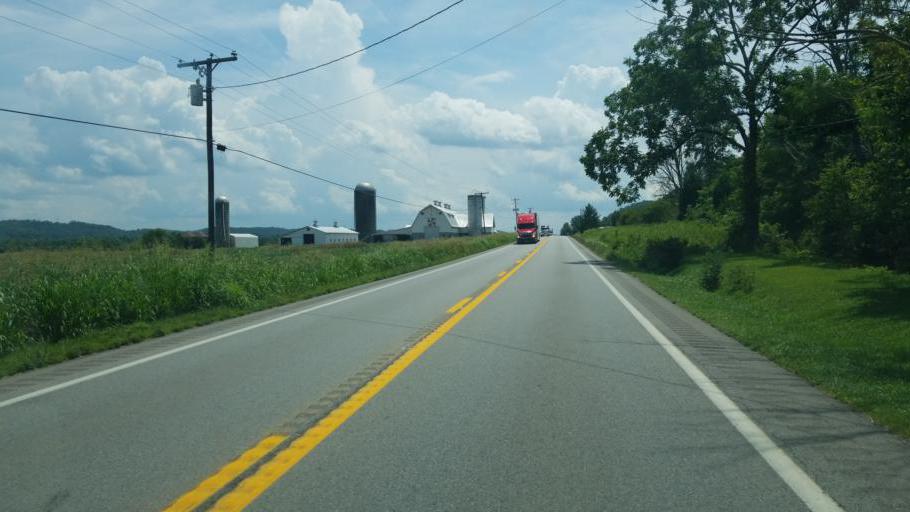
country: US
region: West Virginia
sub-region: Putnam County
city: Buffalo
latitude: 38.7292
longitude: -81.9727
